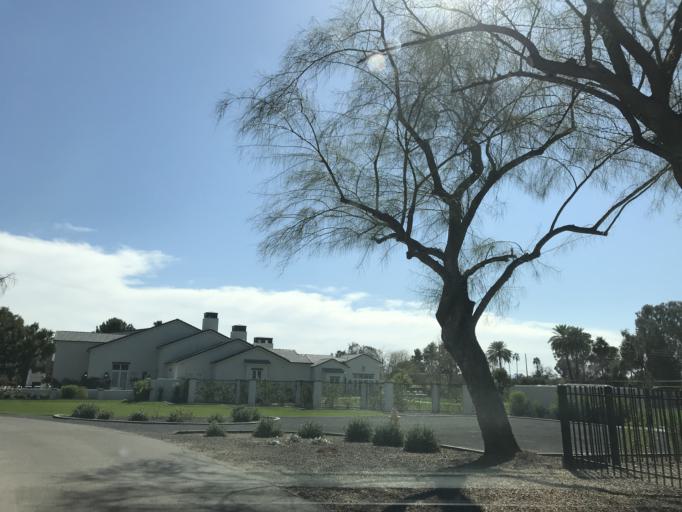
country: US
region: Arizona
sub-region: Maricopa County
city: Phoenix
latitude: 33.5149
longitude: -112.0370
